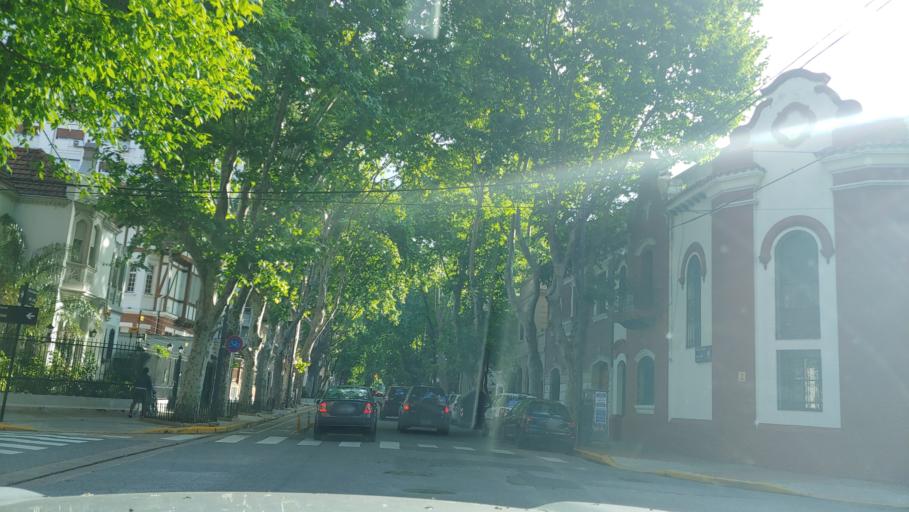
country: AR
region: Buenos Aires F.D.
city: Colegiales
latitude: -34.5658
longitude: -58.4423
